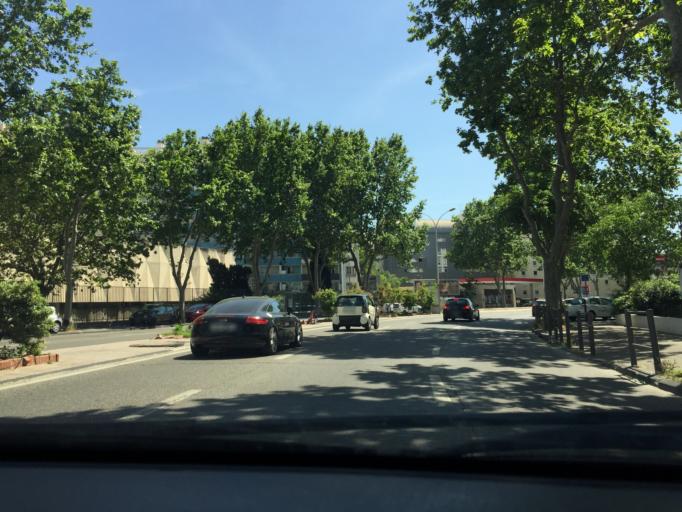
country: FR
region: Provence-Alpes-Cote d'Azur
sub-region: Departement des Bouches-du-Rhone
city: Marseille 05
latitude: 43.2876
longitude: 5.4003
